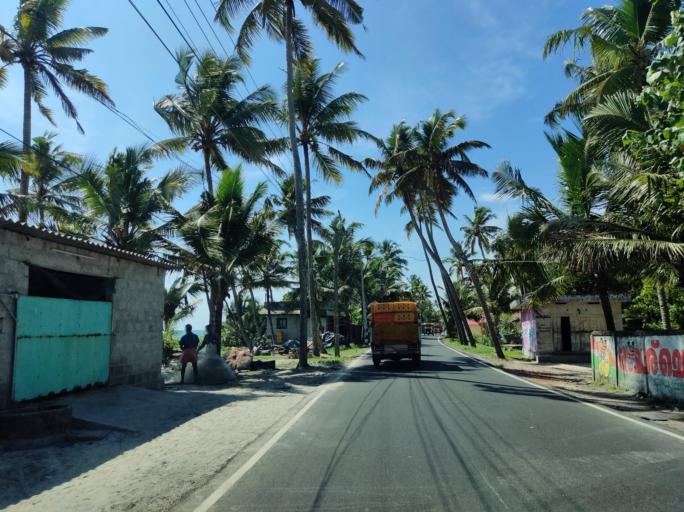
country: IN
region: Kerala
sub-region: Alappuzha
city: Kayankulam
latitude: 9.2562
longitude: 76.4082
